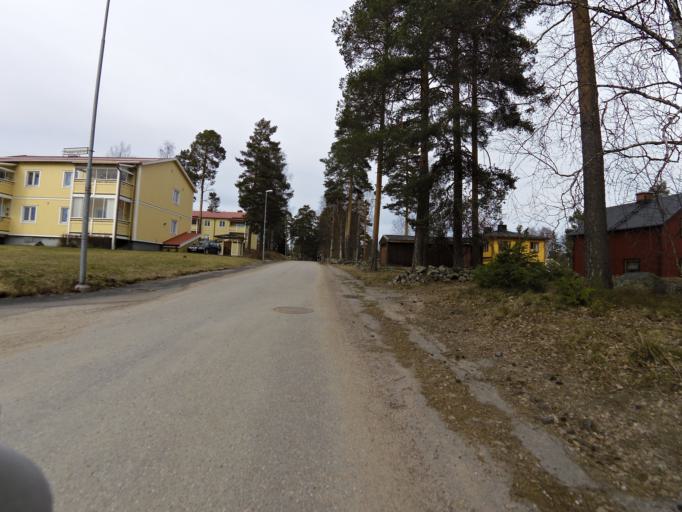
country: SE
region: Gaevleborg
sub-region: Hofors Kommun
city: Hofors
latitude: 60.5482
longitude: 16.2803
